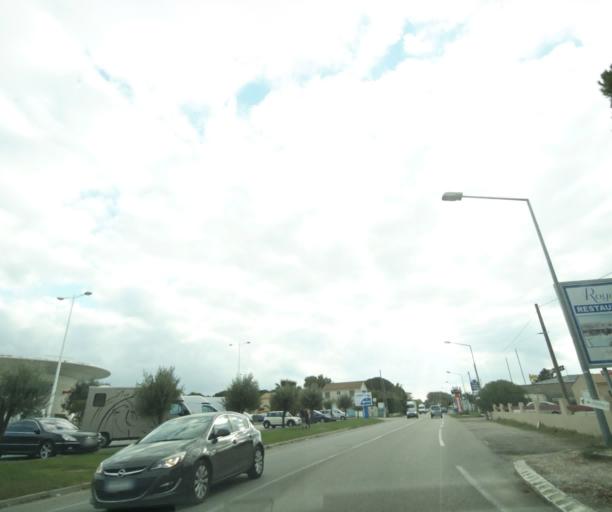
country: FR
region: Languedoc-Roussillon
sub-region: Departement du Gard
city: Aigues-Mortes
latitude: 43.5766
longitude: 4.1984
